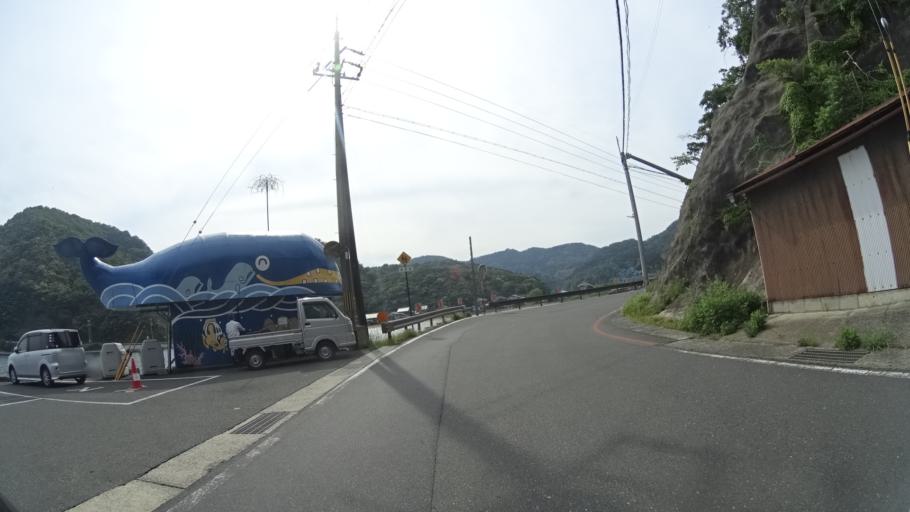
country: JP
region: Kyoto
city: Miyazu
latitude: 35.6701
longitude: 135.2774
